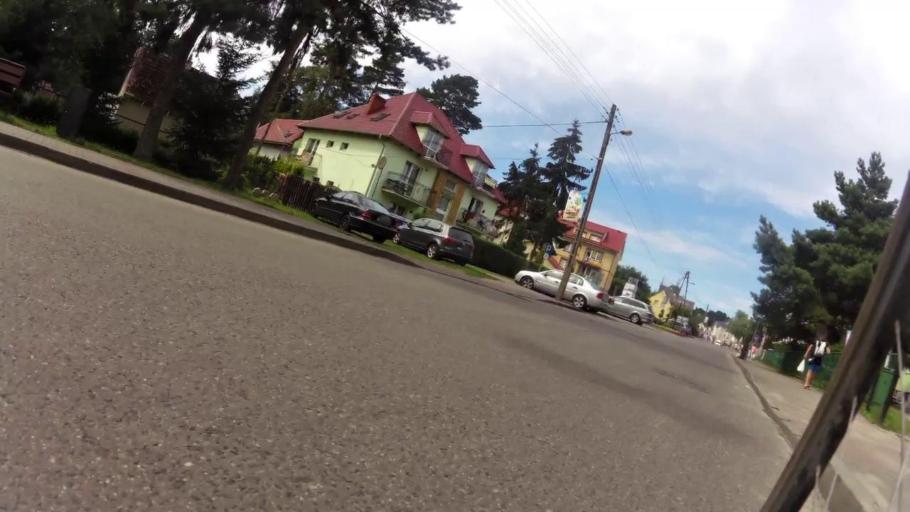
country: PL
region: West Pomeranian Voivodeship
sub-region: Powiat gryficki
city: Pobierowo
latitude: 54.0569
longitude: 14.9281
